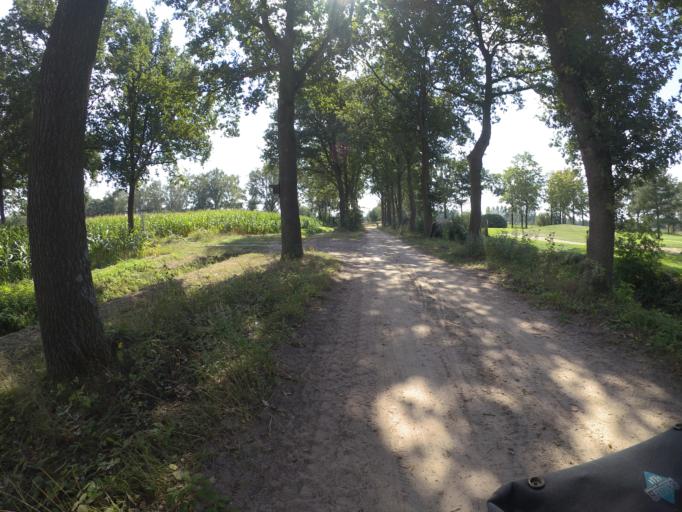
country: NL
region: North Brabant
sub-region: Gemeente Sint-Oedenrode
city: Sint-Oedenrode
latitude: 51.5877
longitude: 5.4385
